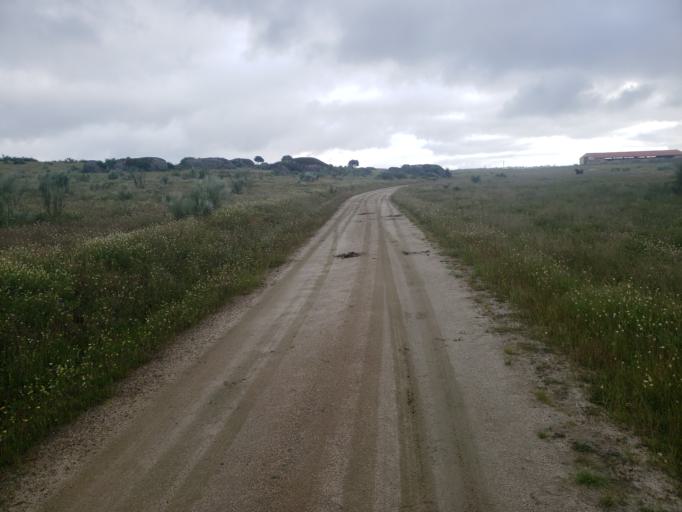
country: ES
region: Extremadura
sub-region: Provincia de Caceres
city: Malpartida de Caceres
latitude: 39.4274
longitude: -6.4931
